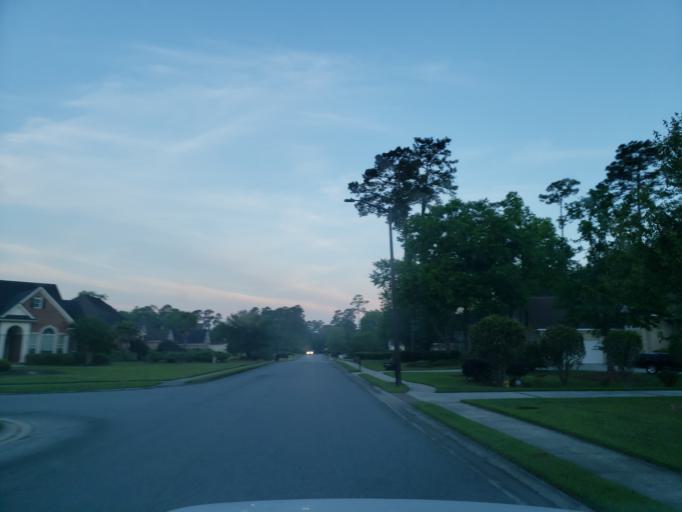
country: US
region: Georgia
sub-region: Chatham County
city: Pooler
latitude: 32.0713
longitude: -81.2297
